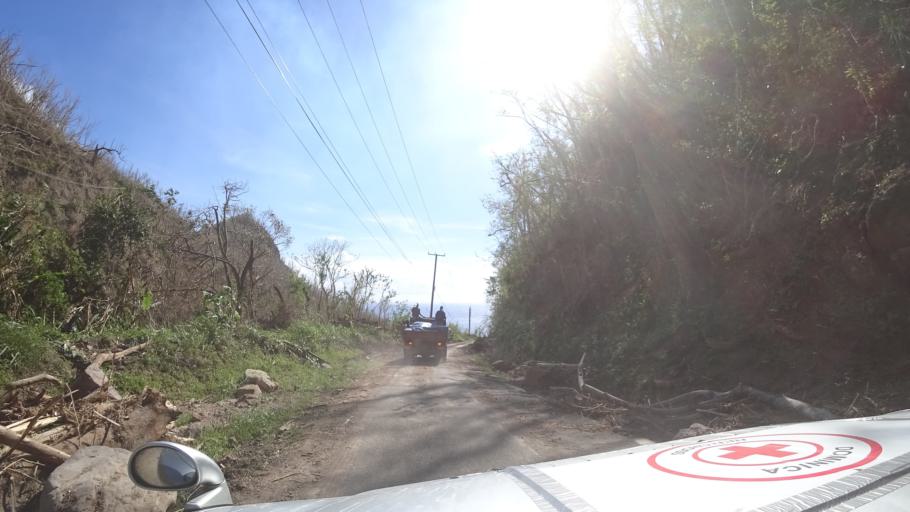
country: DM
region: Saint Mark
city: Soufriere
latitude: 15.2429
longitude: -61.3646
